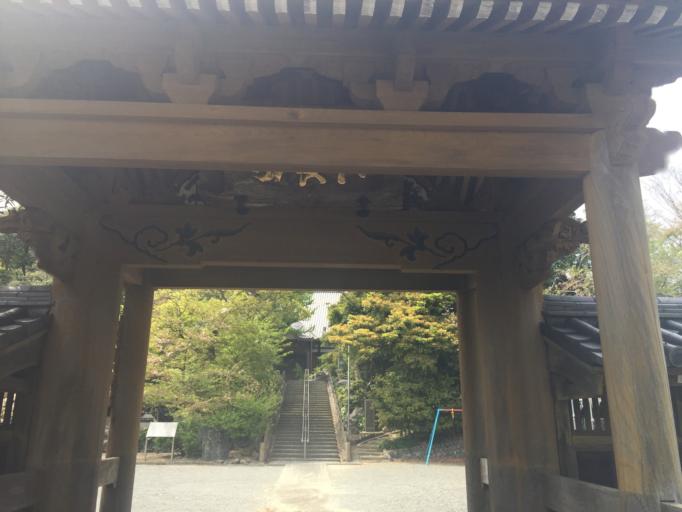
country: JP
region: Shizuoka
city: Kakegawa
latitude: 34.6811
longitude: 138.0627
